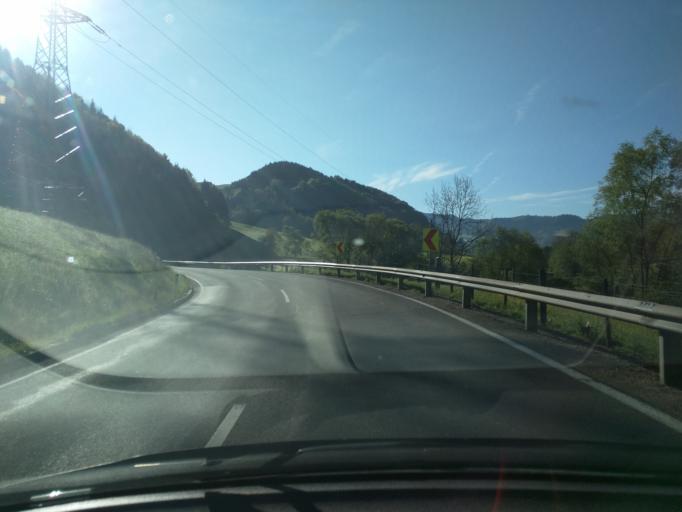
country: AT
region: Lower Austria
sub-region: Politischer Bezirk Scheibbs
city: Randegg
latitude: 48.0028
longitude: 14.9998
